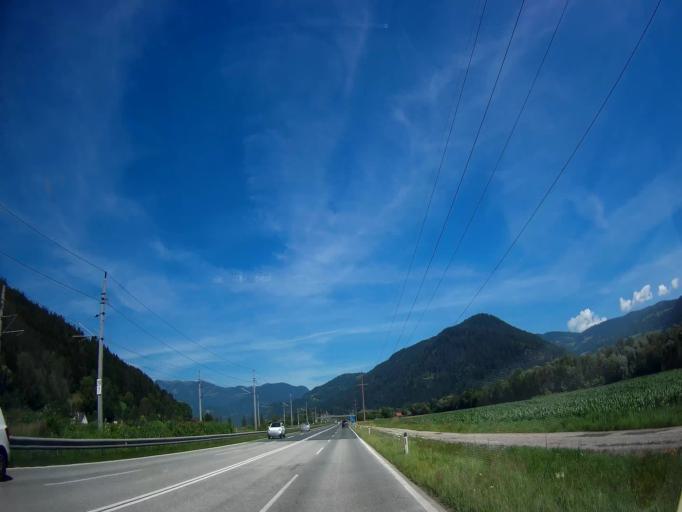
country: AT
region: Carinthia
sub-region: Politischer Bezirk Sankt Veit an der Glan
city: Micheldorf
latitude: 46.9346
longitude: 14.4261
